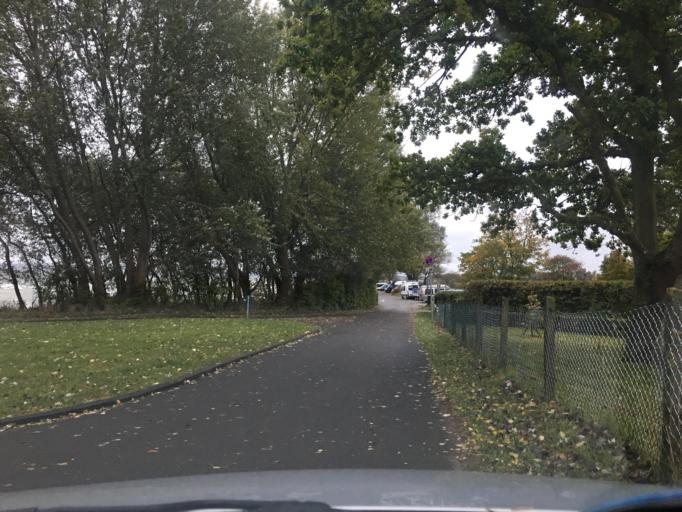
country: DE
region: Schleswig-Holstein
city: Strande
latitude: 54.4551
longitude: 10.1975
